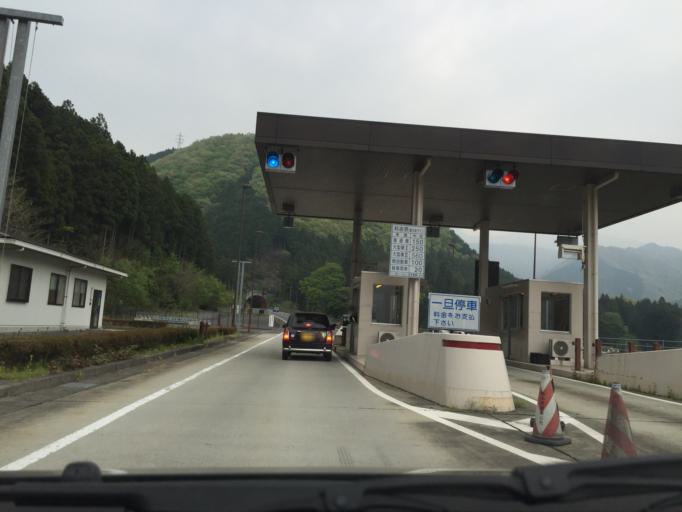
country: JP
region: Tochigi
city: Imaichi
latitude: 36.8469
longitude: 139.7224
